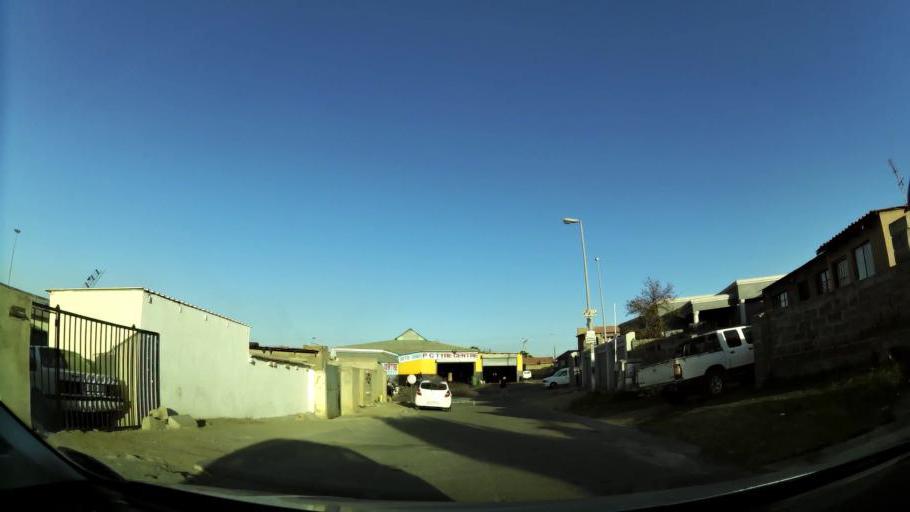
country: ZA
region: Gauteng
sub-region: Ekurhuleni Metropolitan Municipality
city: Tembisa
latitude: -26.0233
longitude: 28.2023
